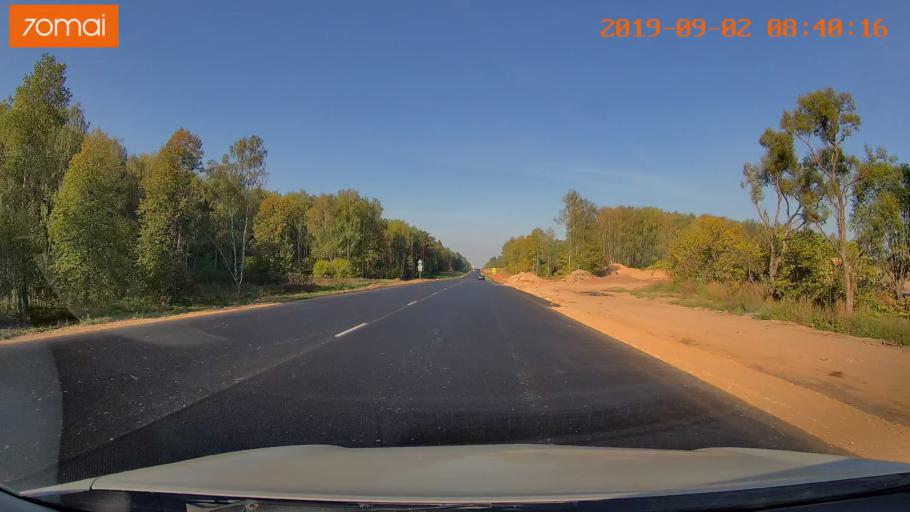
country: RU
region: Kaluga
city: Kudinovo
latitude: 54.9743
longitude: 36.1397
